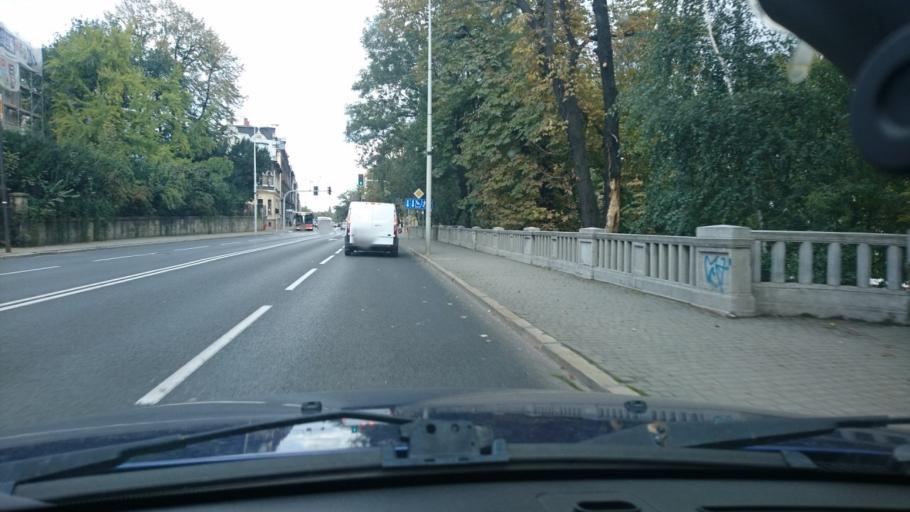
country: PL
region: Silesian Voivodeship
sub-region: Bielsko-Biala
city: Bielsko-Biala
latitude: 49.8253
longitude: 19.0449
